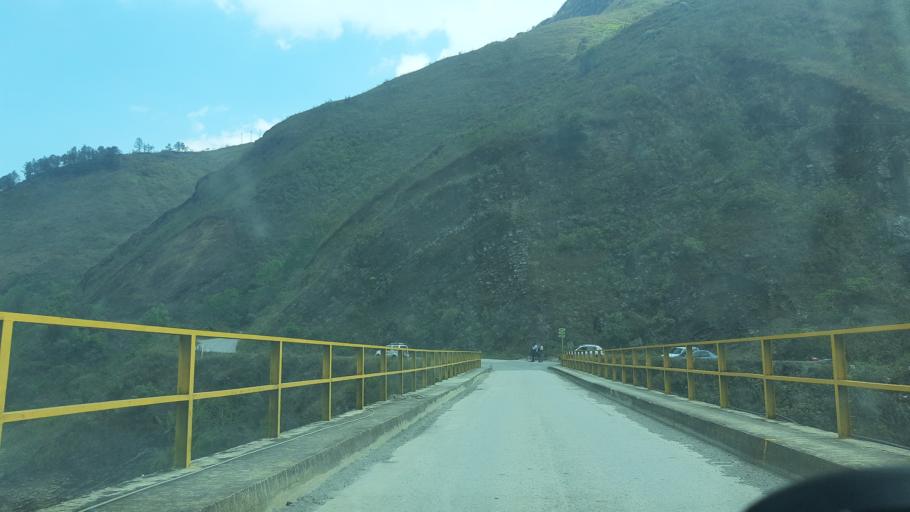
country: CO
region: Boyaca
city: Somondoco
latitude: 5.0164
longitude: -73.3857
